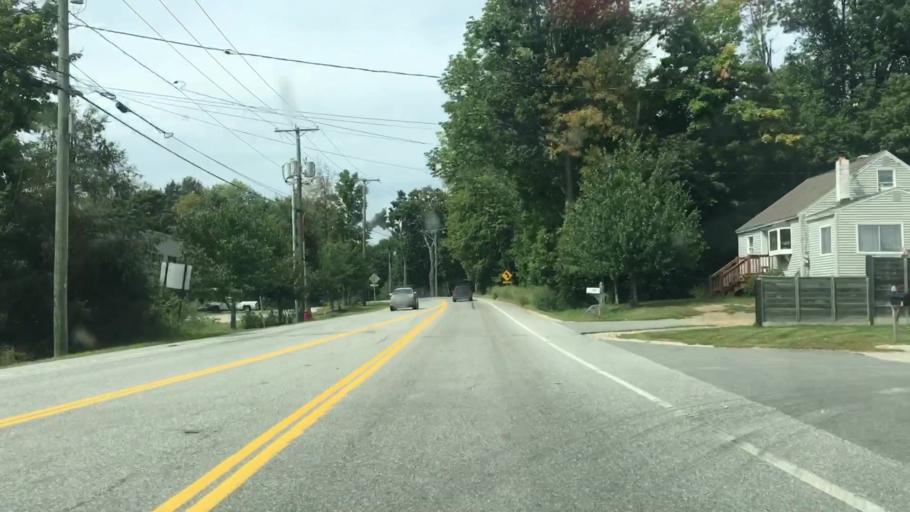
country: US
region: New Hampshire
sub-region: Strafford County
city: Dover
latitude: 43.1881
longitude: -70.8993
